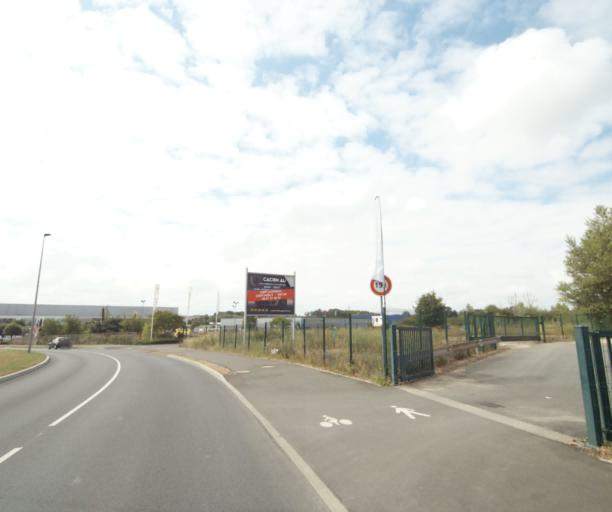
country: FR
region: Centre
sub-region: Departement du Loiret
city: Checy
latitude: 47.9043
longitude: 2.0362
